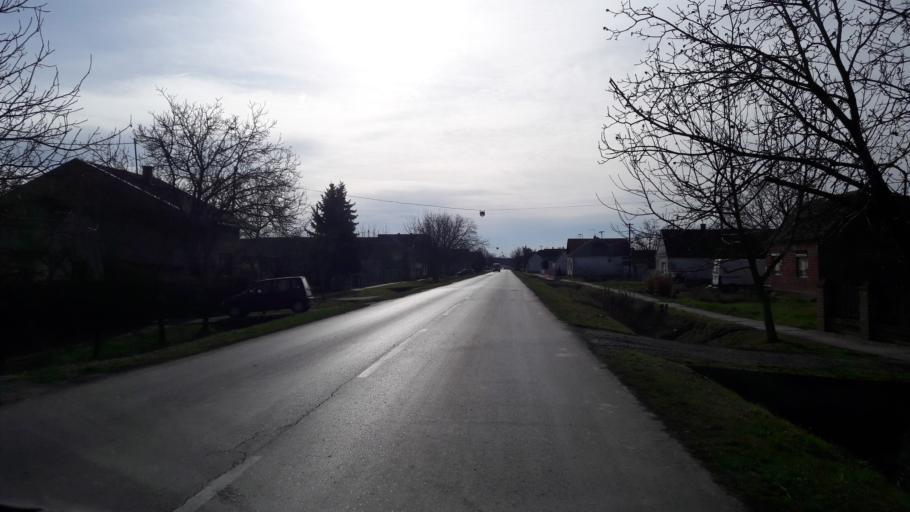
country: HR
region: Osjecko-Baranjska
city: Semeljci
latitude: 45.3127
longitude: 18.5573
